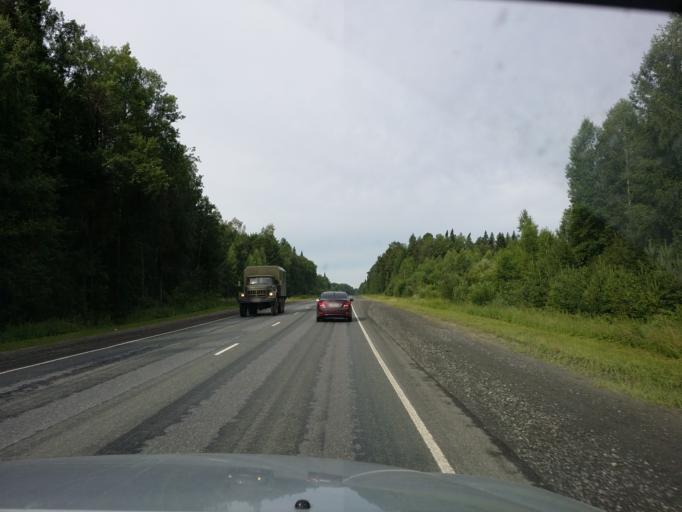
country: RU
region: Tjumen
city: Abalak
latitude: 58.4804
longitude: 68.6266
